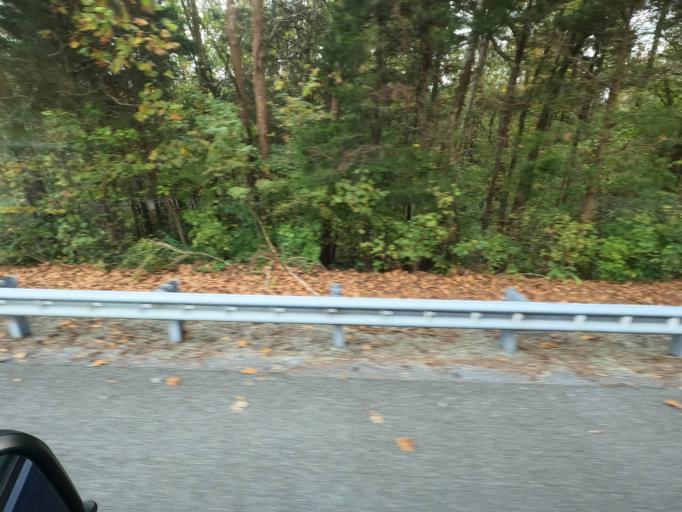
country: US
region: Tennessee
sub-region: Cheatham County
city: Kingston Springs
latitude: 36.0827
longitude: -87.0989
